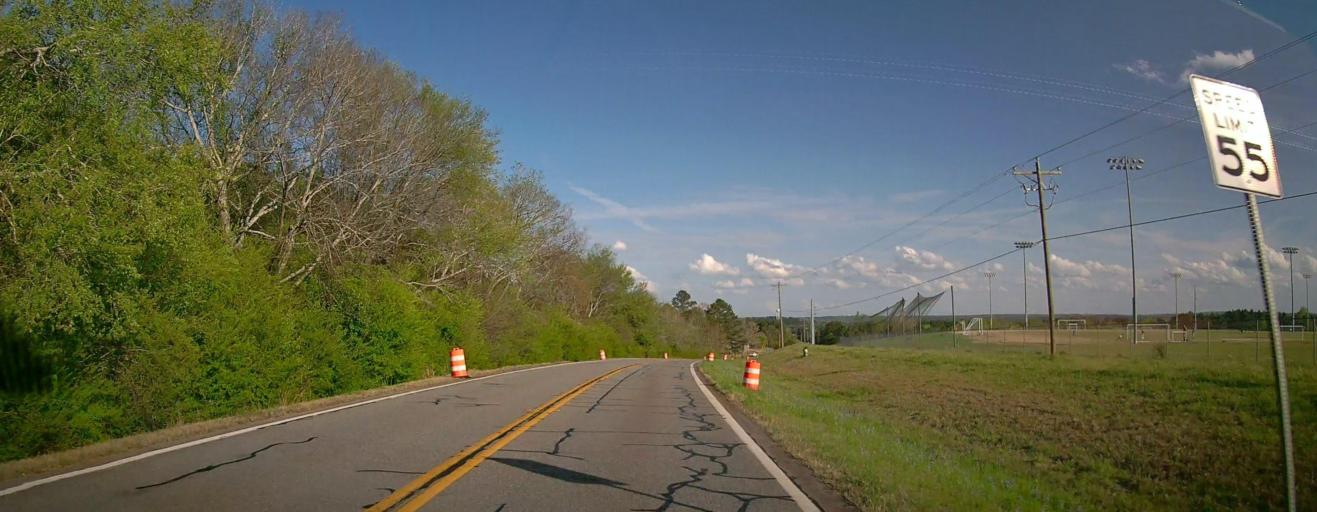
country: US
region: Georgia
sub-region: Baldwin County
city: Milledgeville
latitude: 33.1073
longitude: -83.2797
